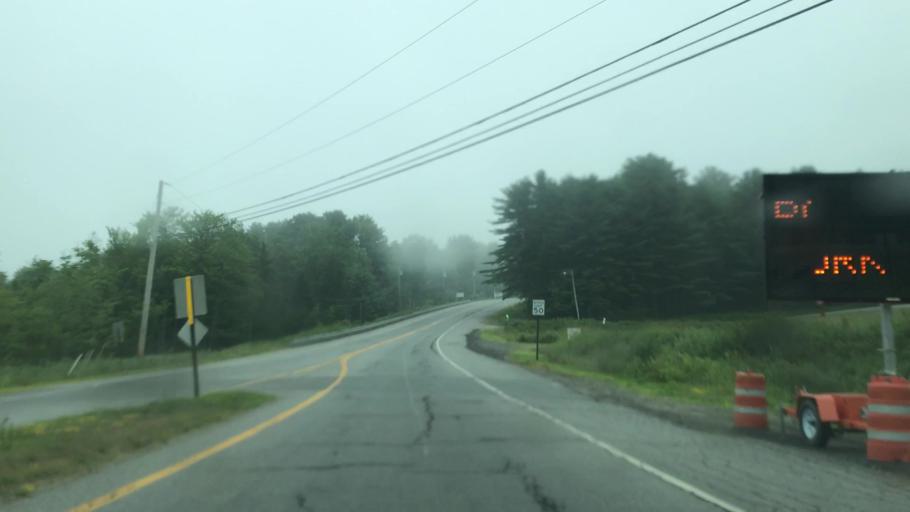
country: US
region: Maine
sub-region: Knox County
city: Warren
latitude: 44.1167
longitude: -69.2629
